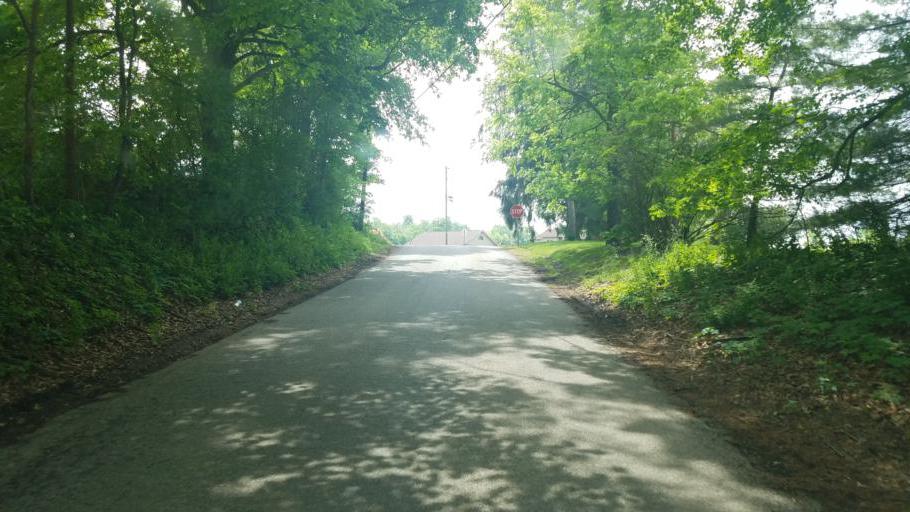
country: US
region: Ohio
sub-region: Licking County
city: Granville
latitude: 40.1161
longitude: -82.5380
